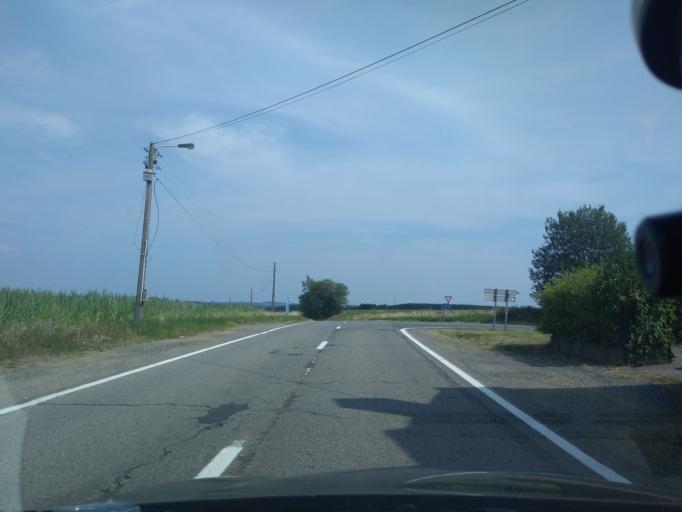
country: BE
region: Wallonia
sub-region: Province du Luxembourg
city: Bertogne
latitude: 50.1479
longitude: 5.7080
